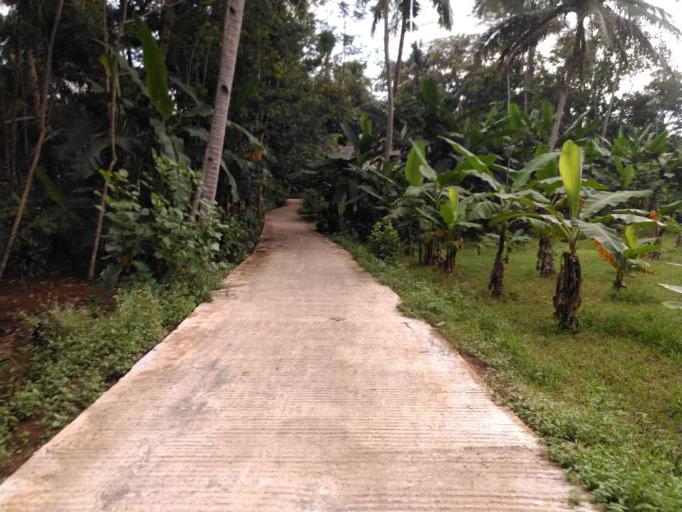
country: ID
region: West Java
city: Cigugur
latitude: -7.6454
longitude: 108.4219
